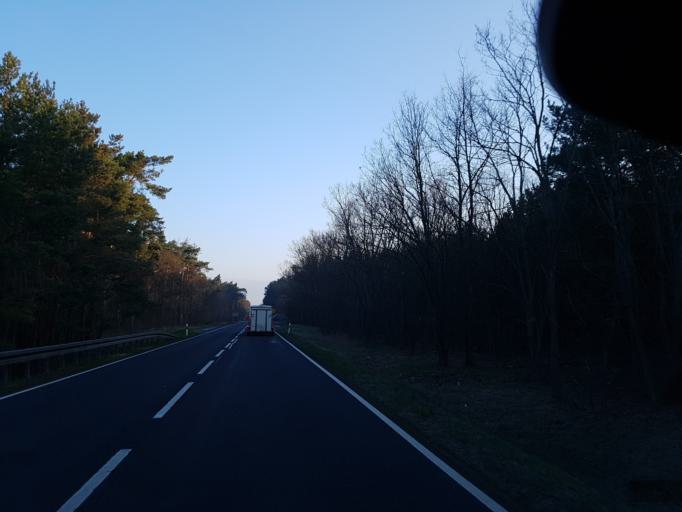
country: DE
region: Saxony-Anhalt
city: Holzdorf
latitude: 51.7707
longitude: 13.1980
